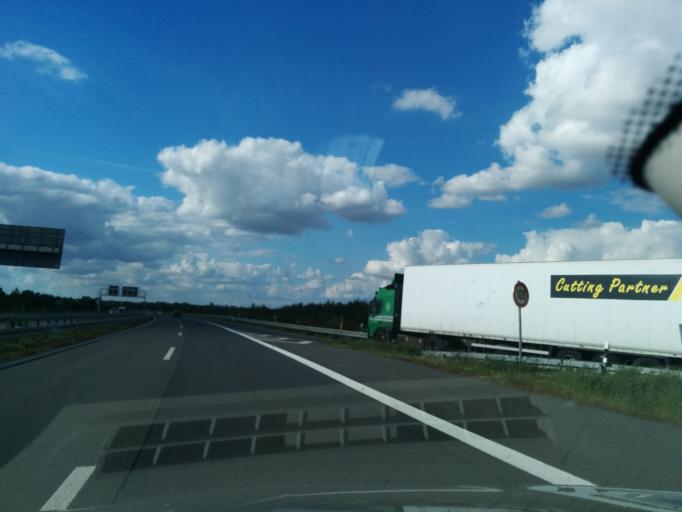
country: DE
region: Brandenburg
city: Gramzow
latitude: 53.2476
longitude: 14.0109
